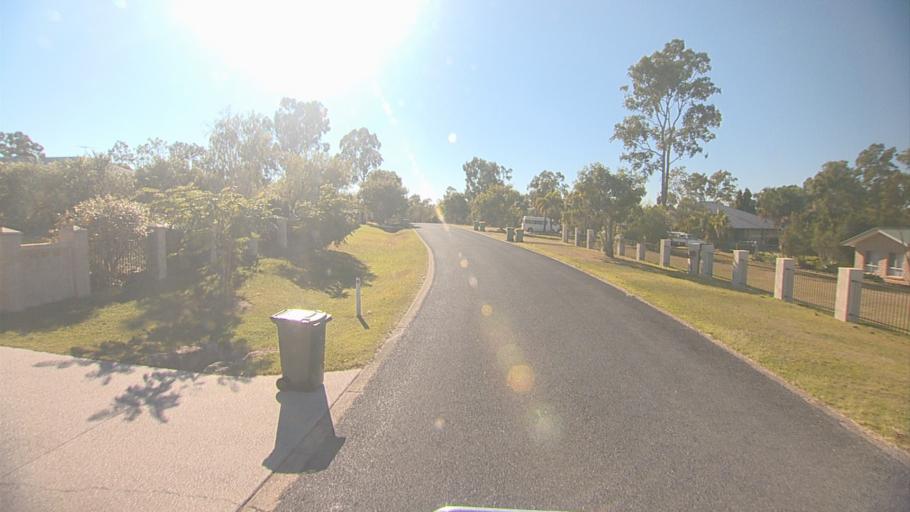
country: AU
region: Queensland
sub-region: Logan
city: North Maclean
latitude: -27.7424
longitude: 152.9609
